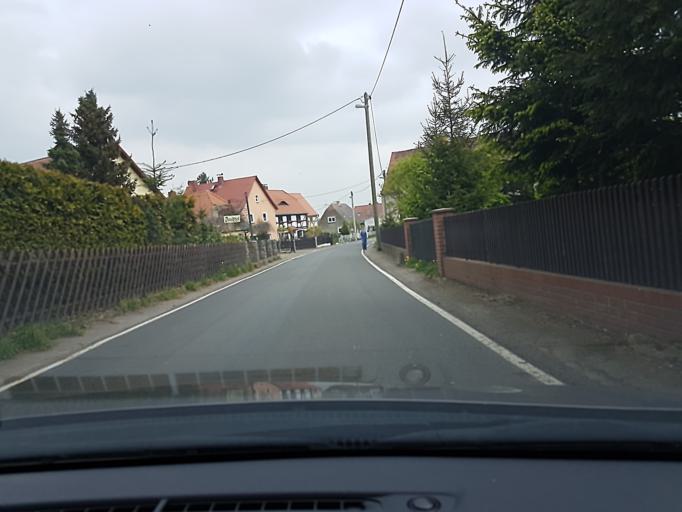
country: DE
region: Saxony
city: Belgern
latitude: 51.4507
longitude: 13.1137
